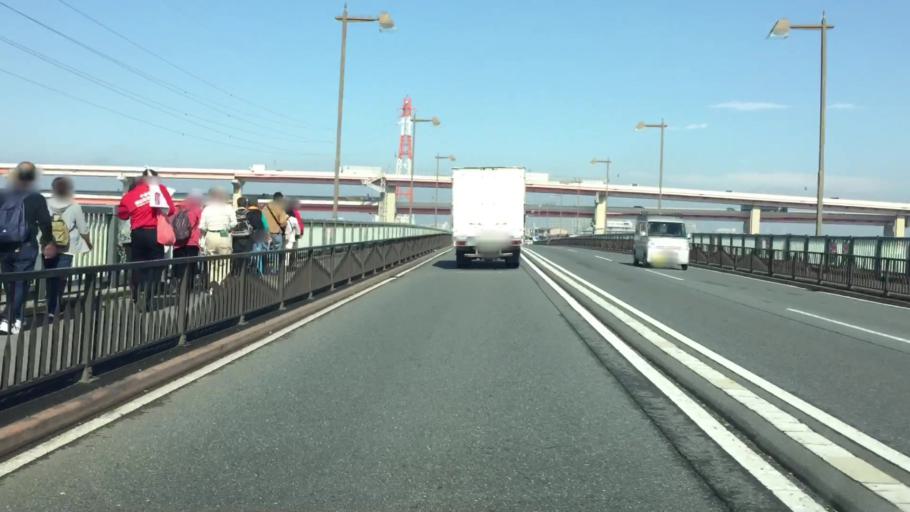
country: JP
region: Saitama
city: Soka
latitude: 35.7579
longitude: 139.7894
